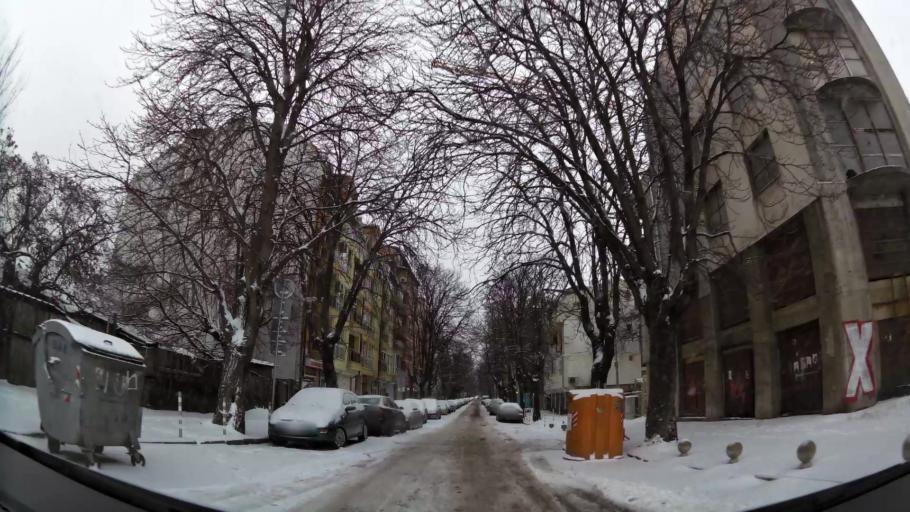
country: BG
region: Sofia-Capital
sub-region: Stolichna Obshtina
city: Sofia
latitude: 42.7056
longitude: 23.3058
